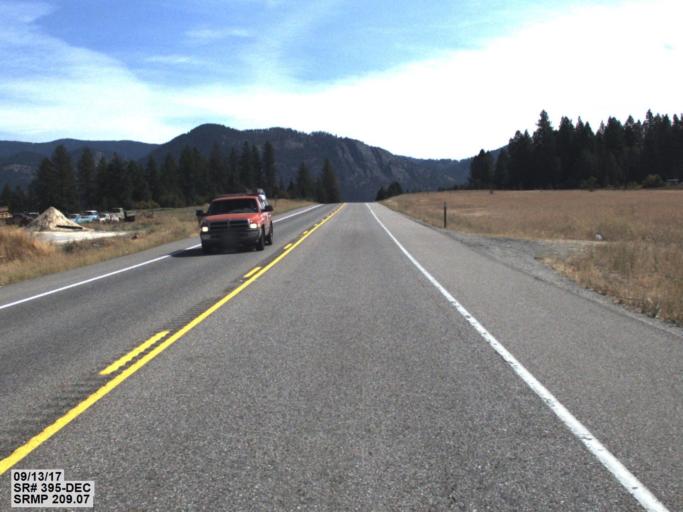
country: US
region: Washington
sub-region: Stevens County
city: Chewelah
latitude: 48.2938
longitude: -117.7425
